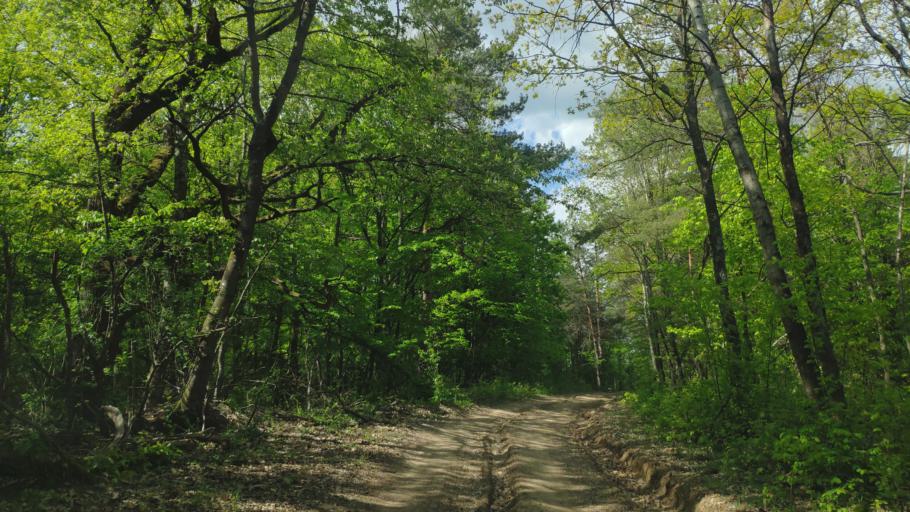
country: SK
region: Kosicky
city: Moldava nad Bodvou
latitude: 48.5552
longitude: 20.9452
